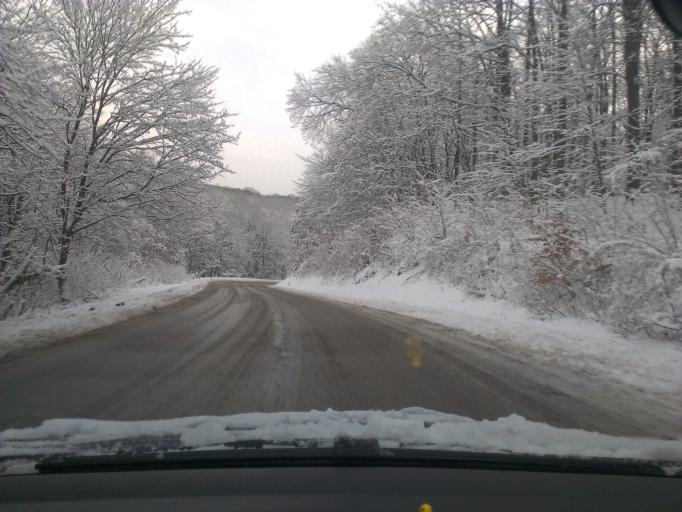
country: SK
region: Trnavsky
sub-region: Okres Trnava
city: Piestany
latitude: 48.5645
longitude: 17.9012
